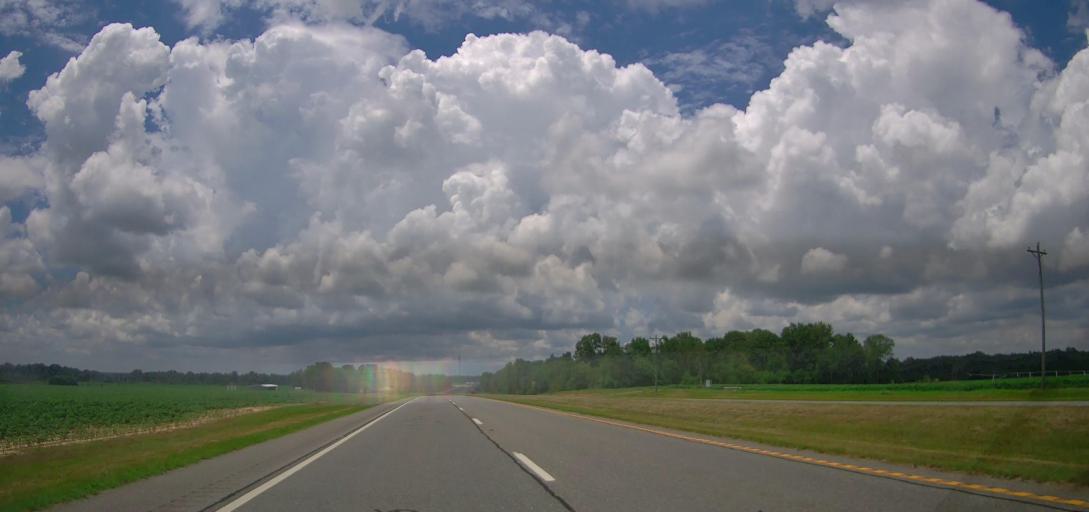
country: US
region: Georgia
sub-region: Pulaski County
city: Hawkinsville
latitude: 32.2352
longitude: -83.3708
